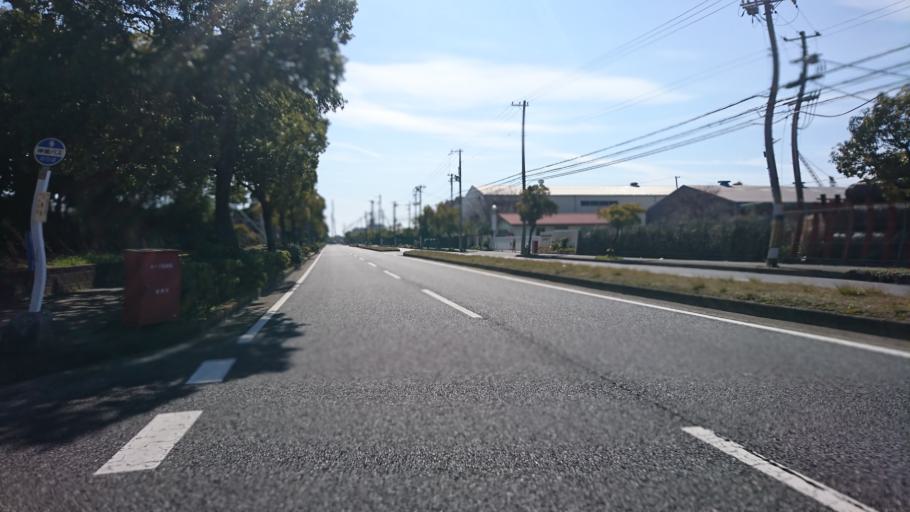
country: JP
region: Hyogo
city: Kakogawacho-honmachi
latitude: 34.7071
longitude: 134.8563
